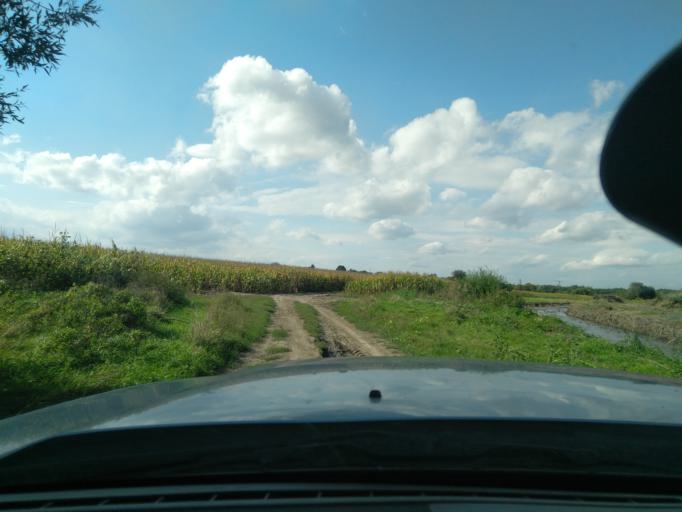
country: HU
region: Fejer
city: Bicske
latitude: 47.4822
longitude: 18.6591
